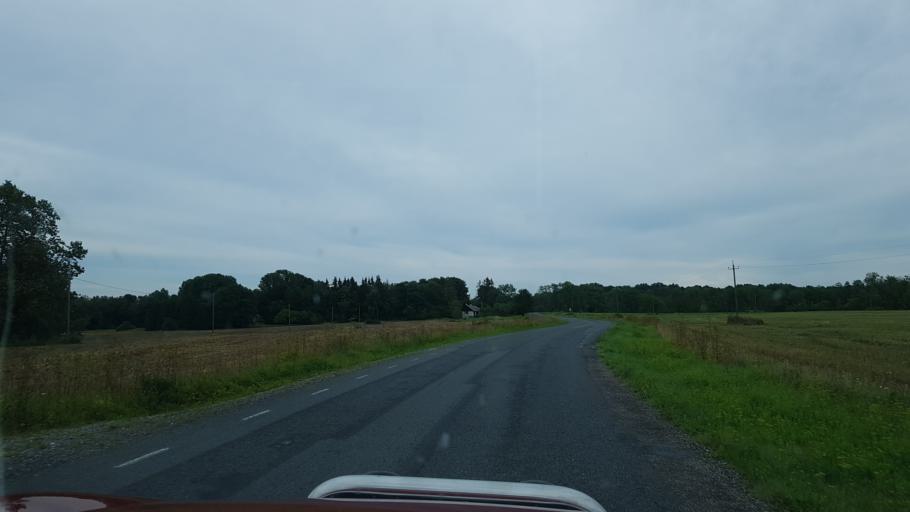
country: EE
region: Laeaene
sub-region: Lihula vald
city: Lihula
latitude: 58.8765
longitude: 23.8635
